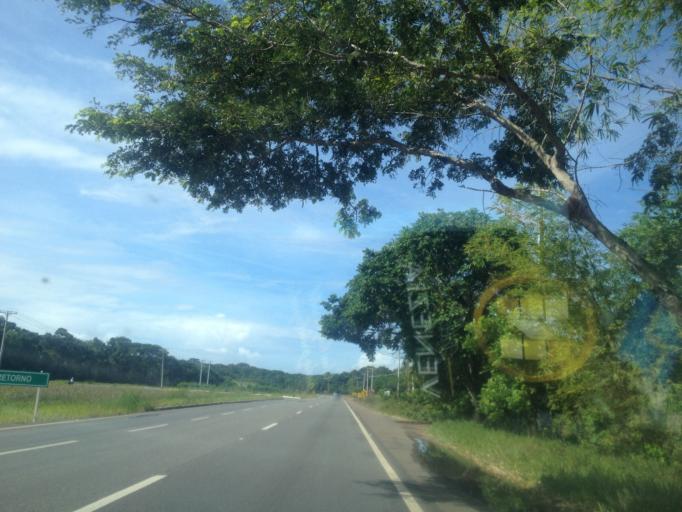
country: BR
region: Bahia
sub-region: Mata De Sao Joao
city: Mata de Sao Joao
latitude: -12.5617
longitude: -38.0143
